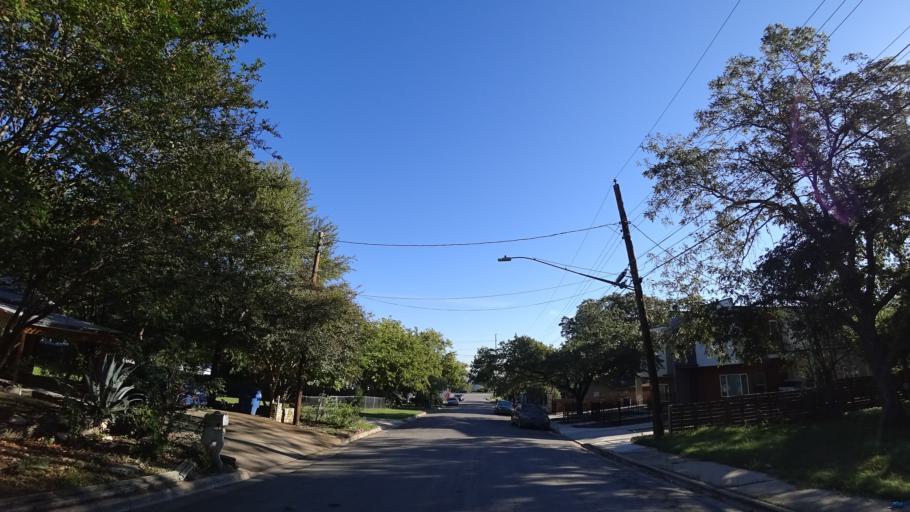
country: US
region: Texas
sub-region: Travis County
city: Austin
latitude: 30.2197
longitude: -97.6952
